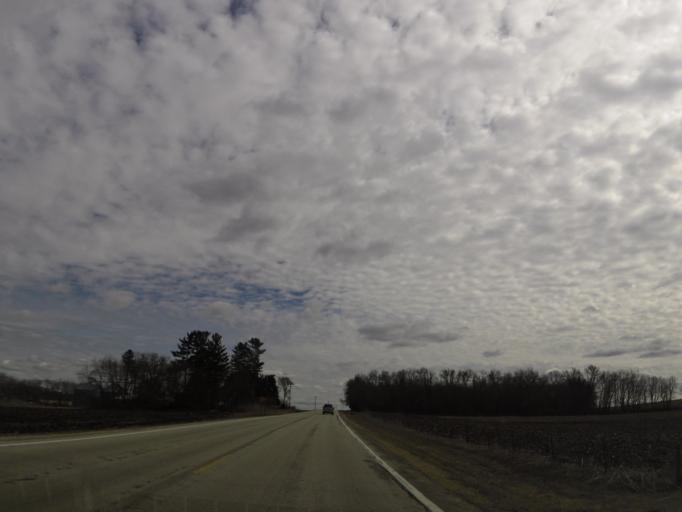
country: US
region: Minnesota
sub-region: Olmsted County
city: Stewartville
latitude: 43.8790
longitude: -92.4047
